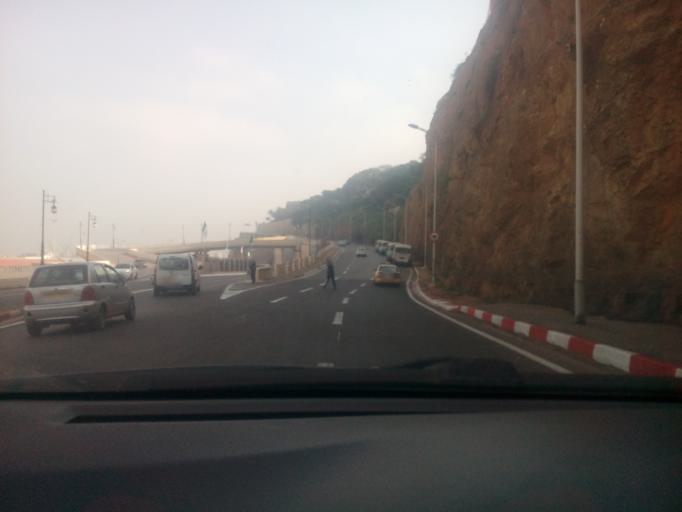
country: DZ
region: Oran
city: Oran
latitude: 35.7073
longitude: -0.6510
